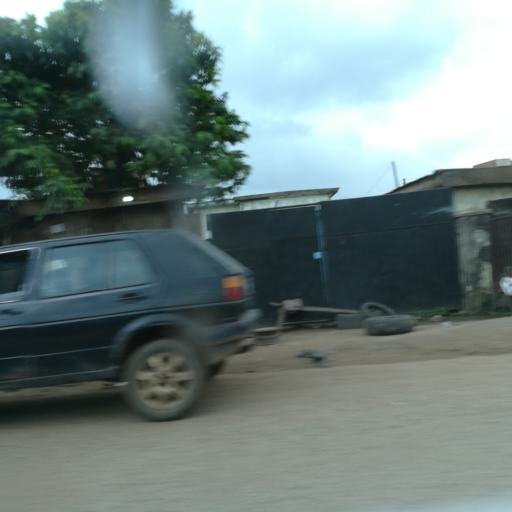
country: NG
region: Lagos
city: Agege
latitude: 6.6104
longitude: 3.3044
